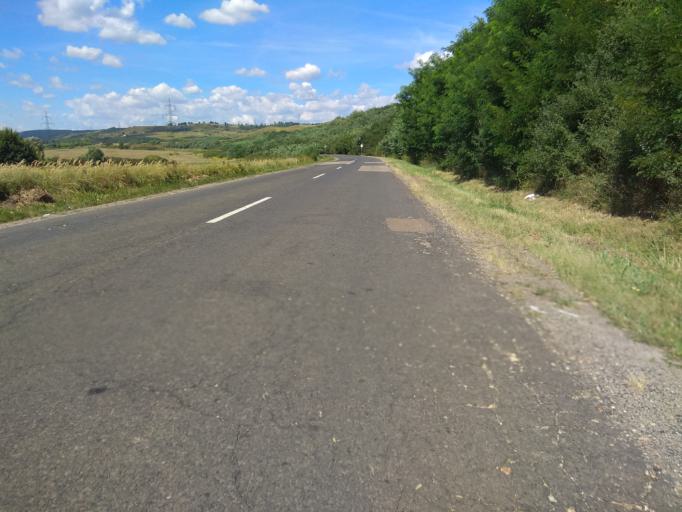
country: HU
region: Borsod-Abauj-Zemplen
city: Sajokaza
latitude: 48.2855
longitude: 20.6202
